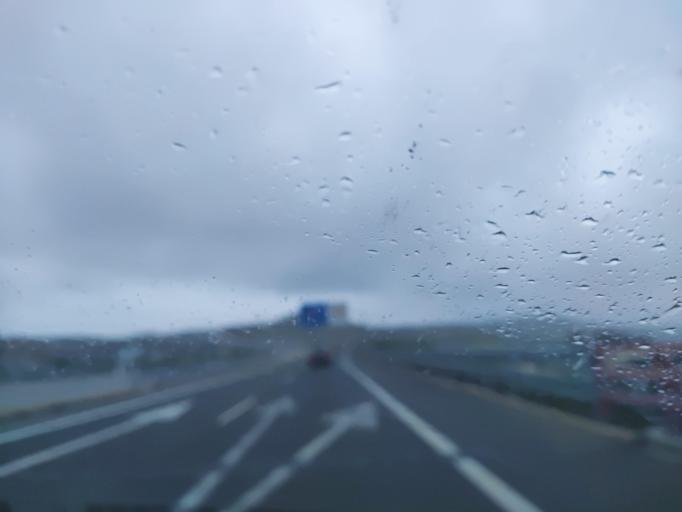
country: ES
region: Castille-La Mancha
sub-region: Province of Toledo
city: Toledo
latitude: 39.8666
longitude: -4.0887
